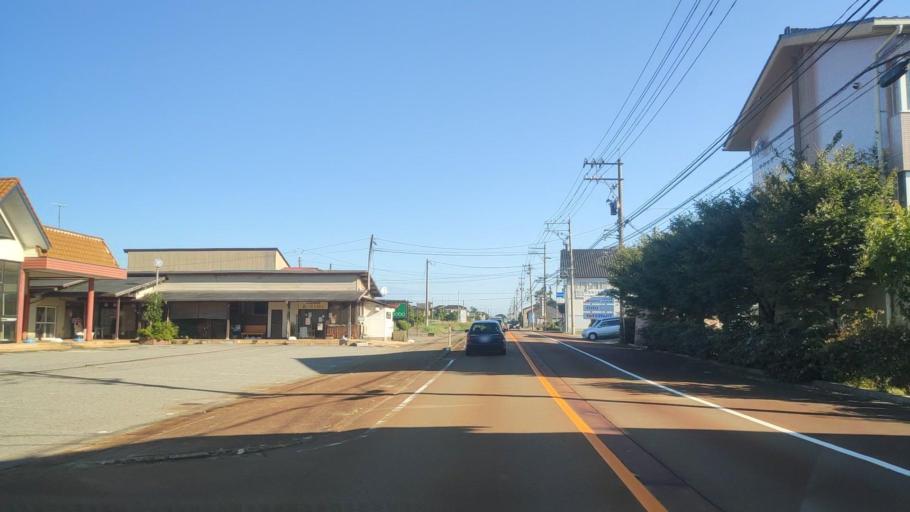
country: JP
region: Ishikawa
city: Hakui
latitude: 36.8524
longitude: 136.7693
